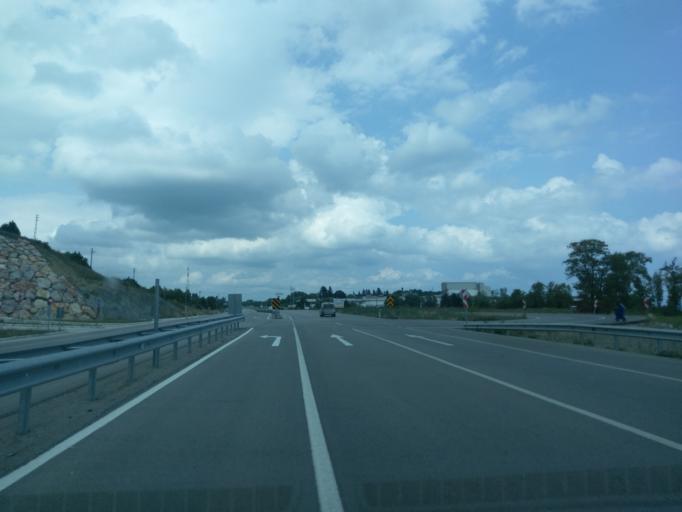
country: TR
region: Sinop
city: Gerze
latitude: 41.8322
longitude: 35.1588
